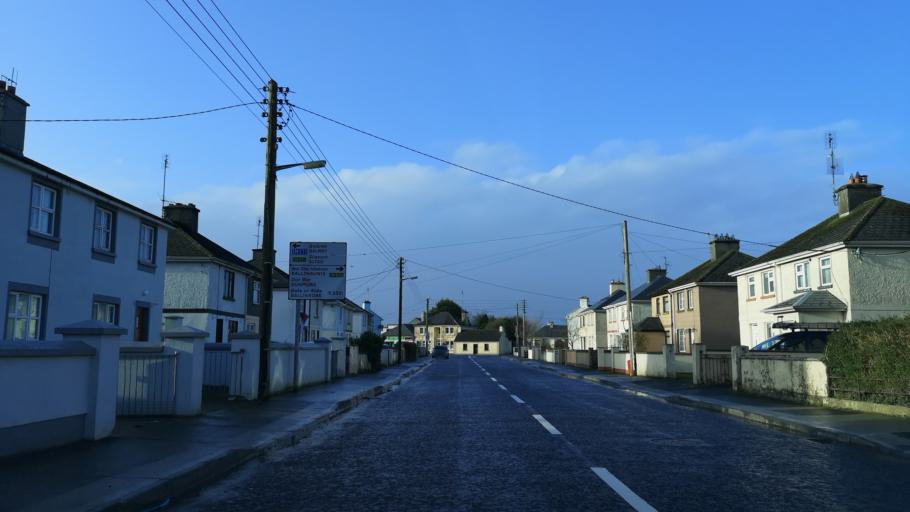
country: IE
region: Connaught
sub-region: County Galway
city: Tuam
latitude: 53.5109
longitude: -8.8592
